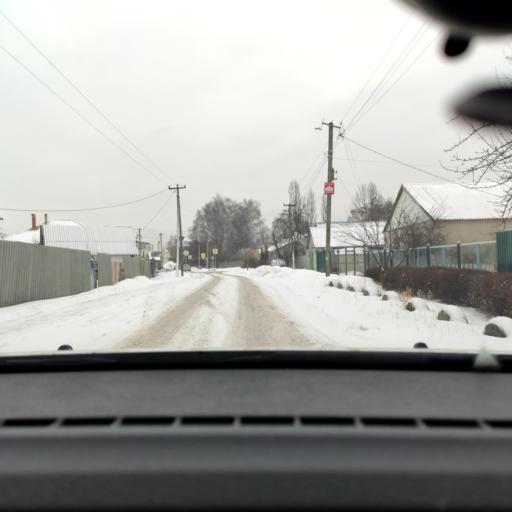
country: RU
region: Voronezj
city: Podgornoye
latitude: 51.7931
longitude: 39.1460
